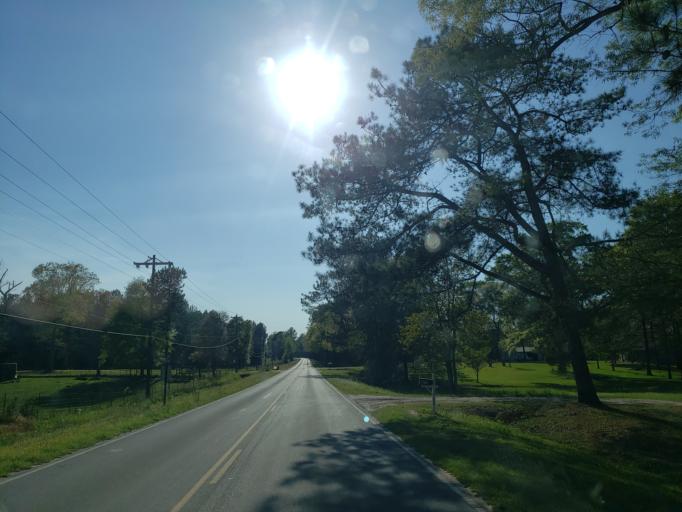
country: US
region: Mississippi
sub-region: Perry County
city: Richton
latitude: 31.4816
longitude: -89.0373
